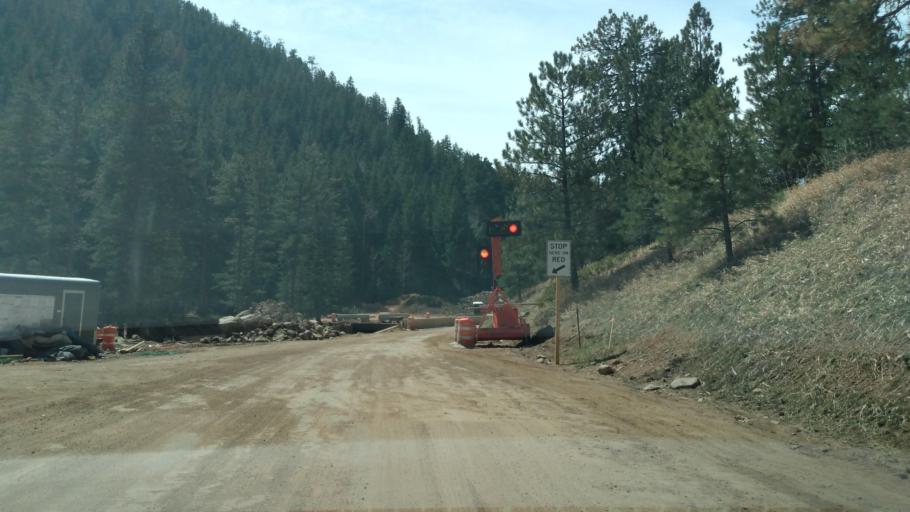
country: US
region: Colorado
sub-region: Boulder County
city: Lyons
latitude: 40.2859
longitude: -105.3798
